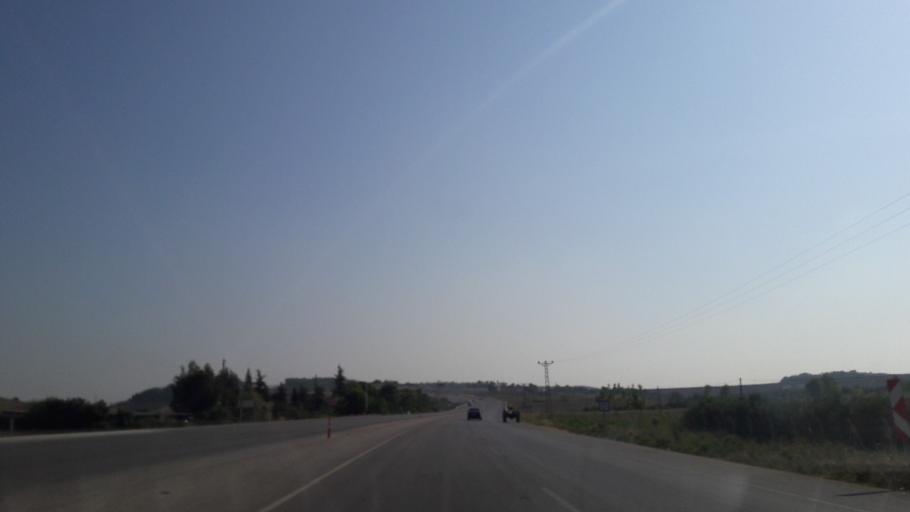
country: TR
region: Adana
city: Yuregir
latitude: 37.0729
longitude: 35.4618
